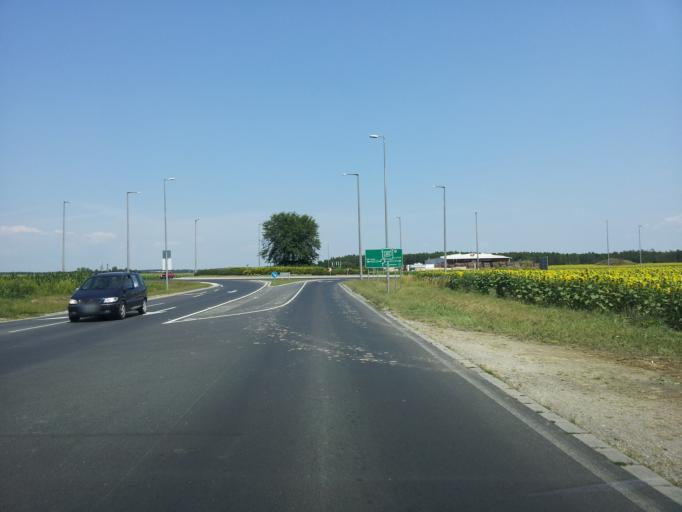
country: HU
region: Zala
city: Zalaegerszeg
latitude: 46.8697
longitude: 16.7944
